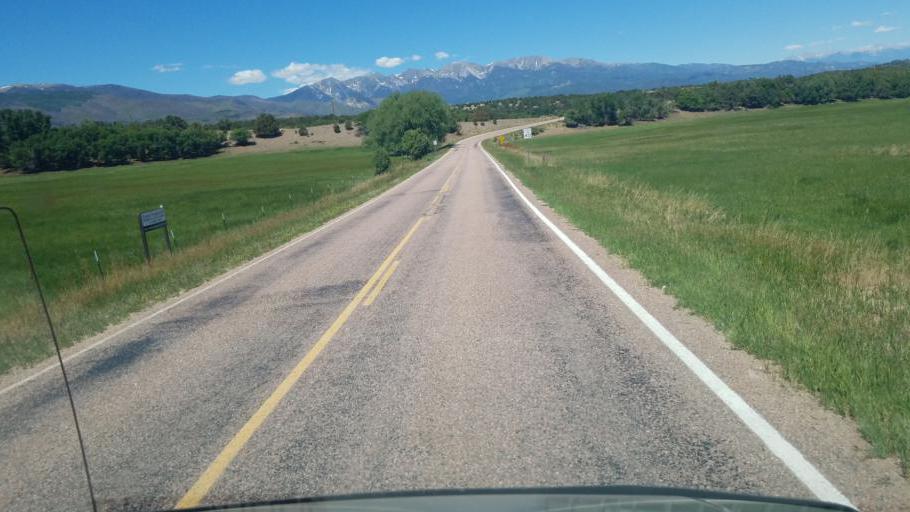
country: US
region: Colorado
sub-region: Custer County
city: Westcliffe
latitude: 38.3121
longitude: -105.6552
